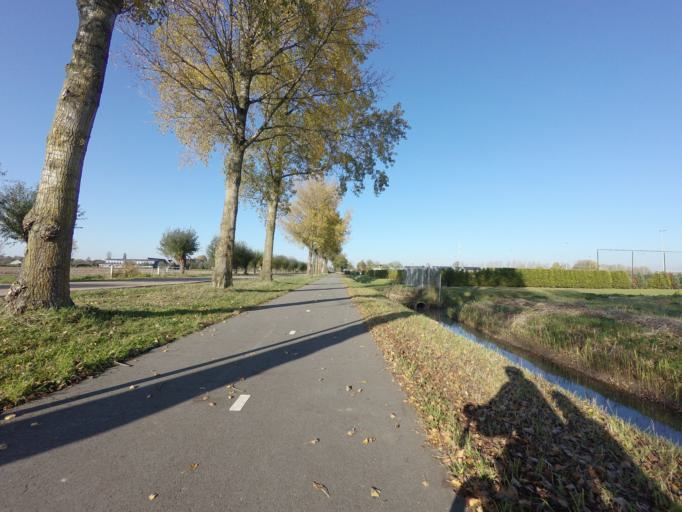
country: NL
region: North Brabant
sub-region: Gemeente Waalwijk
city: Waalwijk
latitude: 51.7266
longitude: 5.0558
